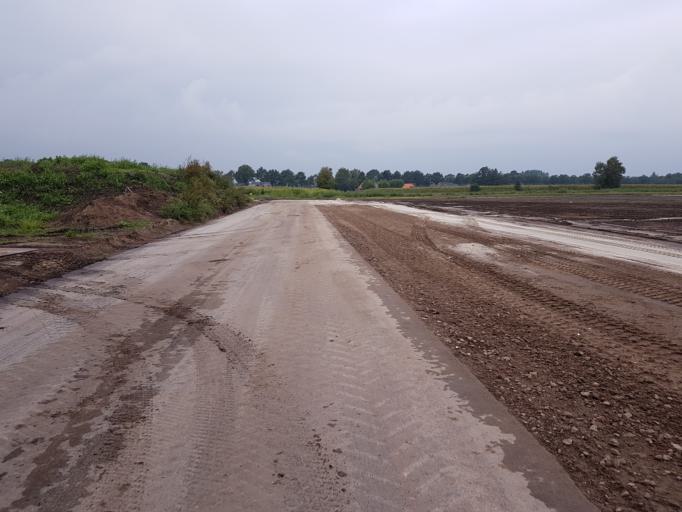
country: NL
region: Overijssel
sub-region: Gemeente Dalfsen
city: Dalfsen
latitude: 52.5813
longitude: 6.2751
